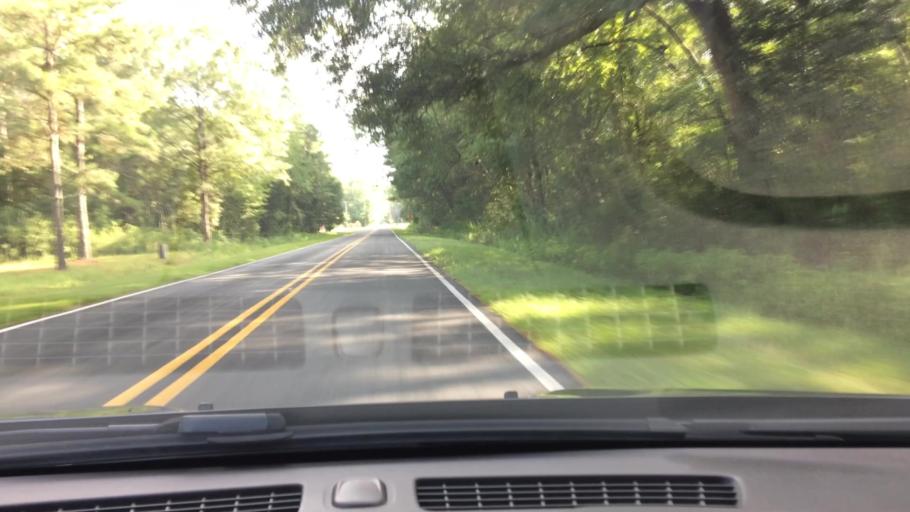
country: US
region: North Carolina
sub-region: Craven County
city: Vanceboro
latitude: 35.4331
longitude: -77.1251
